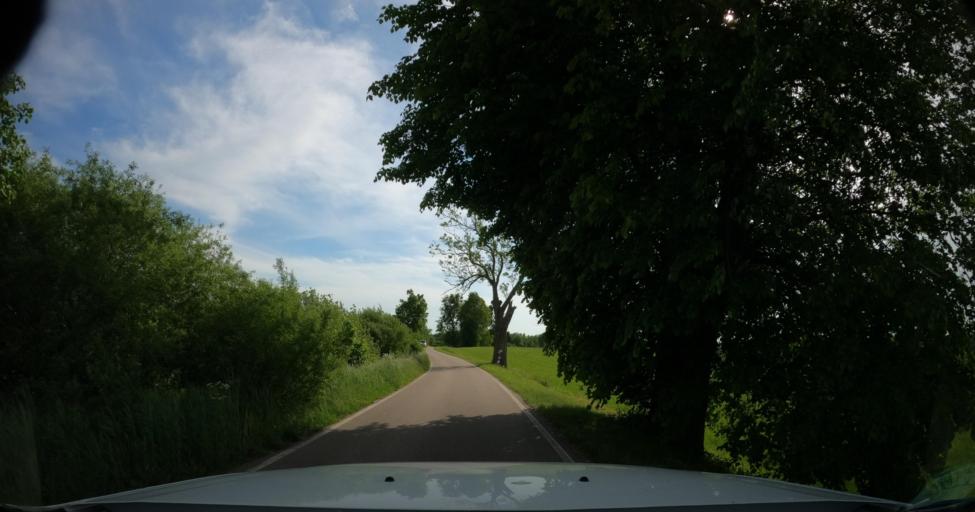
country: PL
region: Warmian-Masurian Voivodeship
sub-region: Powiat ostrodzki
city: Milakowo
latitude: 54.0158
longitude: 20.1544
